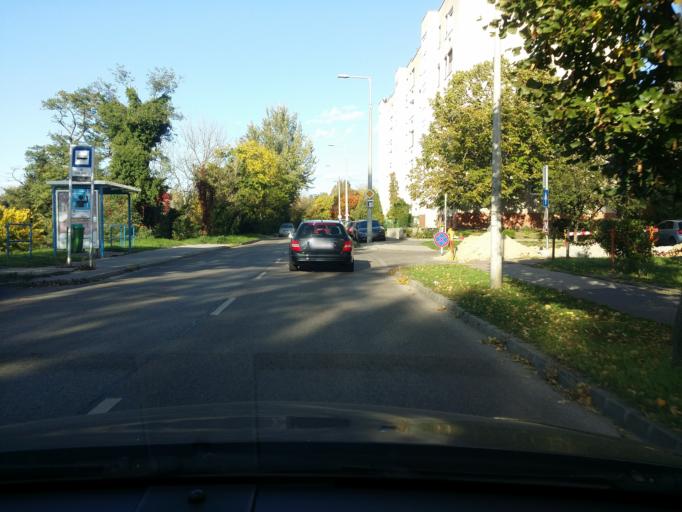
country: HU
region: Budapest
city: Budapest IV. keruelet
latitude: 47.5799
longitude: 19.0958
